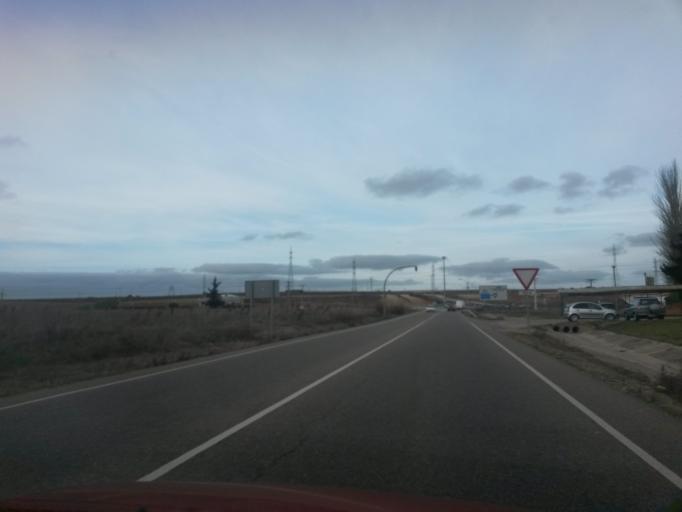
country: ES
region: Castille and Leon
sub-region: Provincia de Salamanca
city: Villares de la Reina
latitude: 40.9959
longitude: -5.6574
